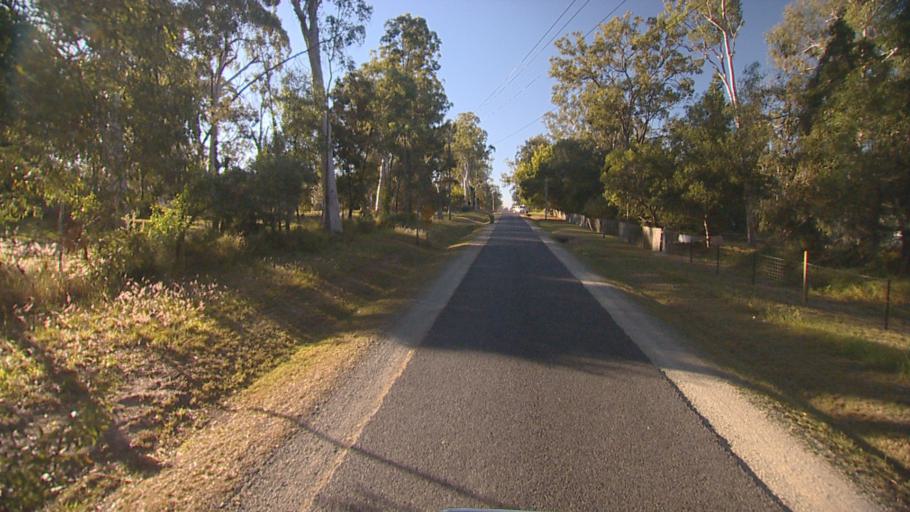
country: AU
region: Queensland
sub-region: Logan
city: Chambers Flat
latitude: -27.7890
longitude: 153.0857
